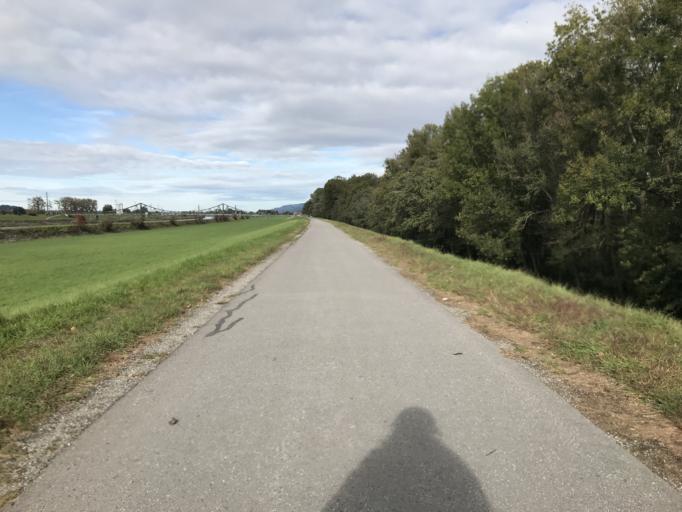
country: CH
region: Saint Gallen
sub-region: Wahlkreis Rheintal
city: Diepoldsau
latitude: 47.3773
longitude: 9.6390
